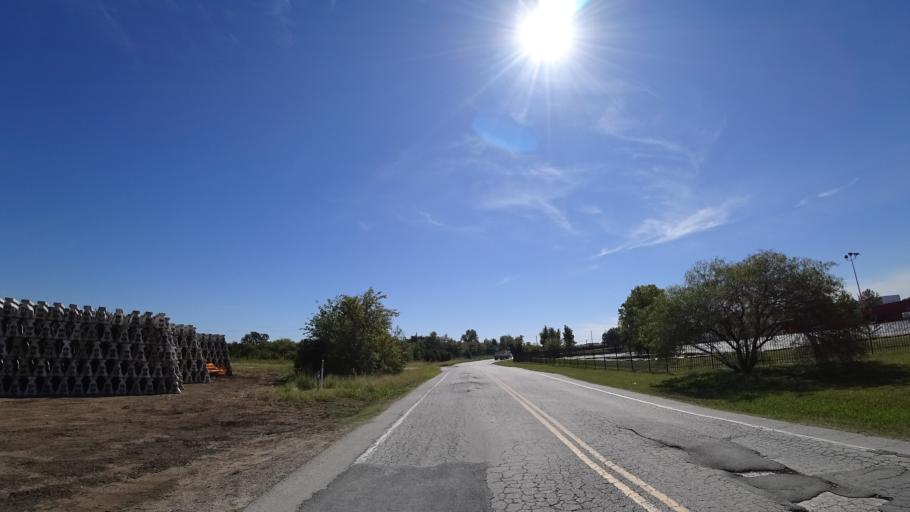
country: US
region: Texas
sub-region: Travis County
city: Austin
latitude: 30.1890
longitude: -97.7030
